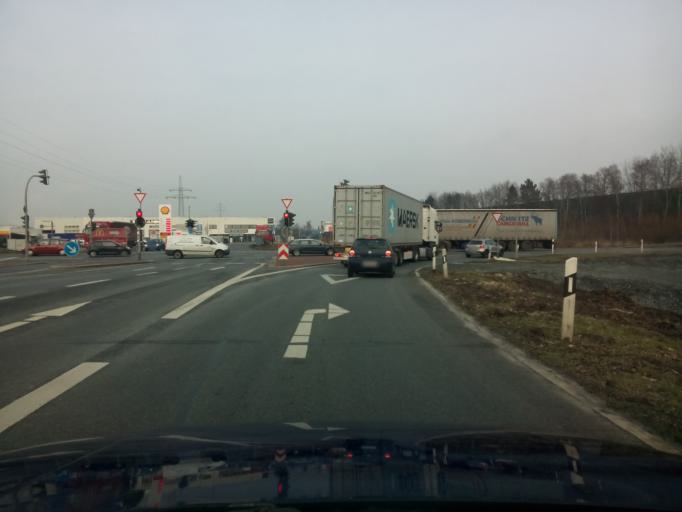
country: DE
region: Lower Saxony
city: Loxstedt
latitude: 53.4959
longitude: 8.6247
